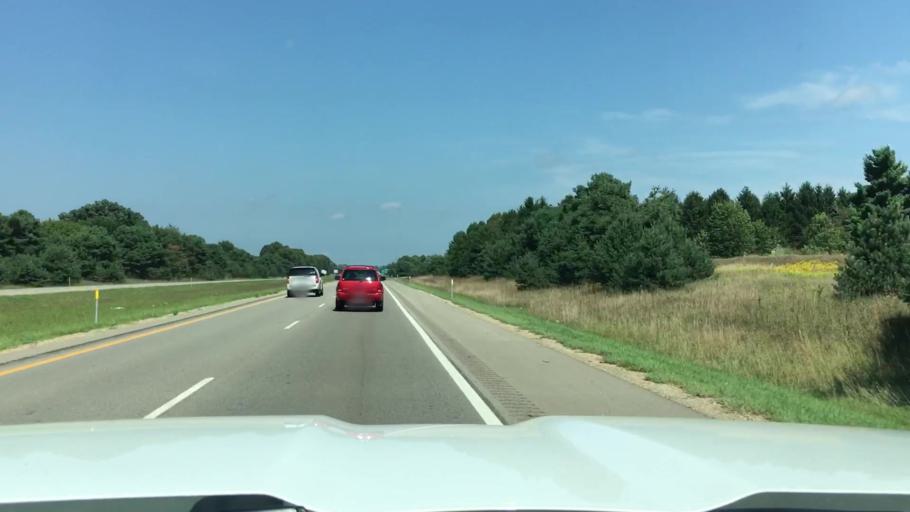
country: US
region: Michigan
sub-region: Kalamazoo County
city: Portage
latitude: 42.2101
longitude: -85.6431
